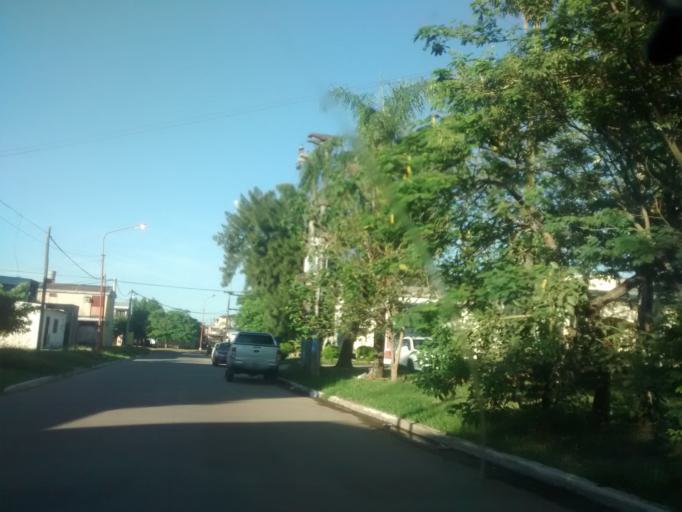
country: AR
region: Chaco
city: Resistencia
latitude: -27.4589
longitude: -59.0169
